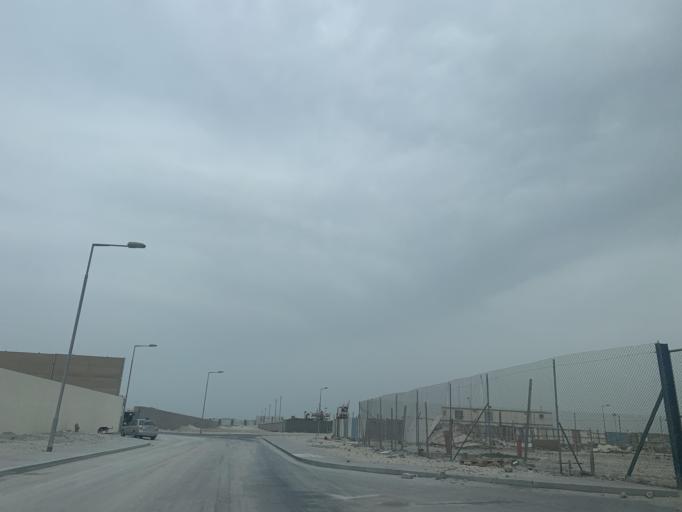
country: BH
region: Muharraq
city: Al Hadd
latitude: 26.2148
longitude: 50.6813
